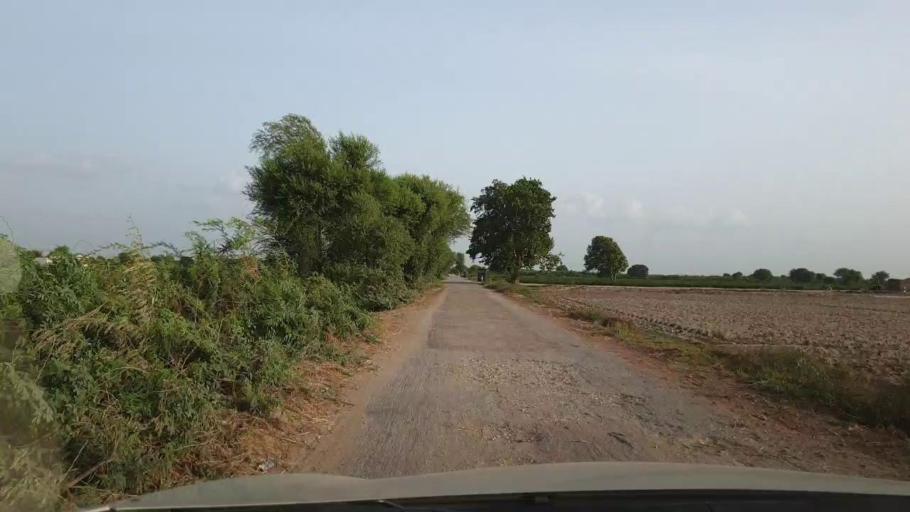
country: PK
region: Sindh
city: Tando Ghulam Ali
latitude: 25.1065
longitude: 68.8849
